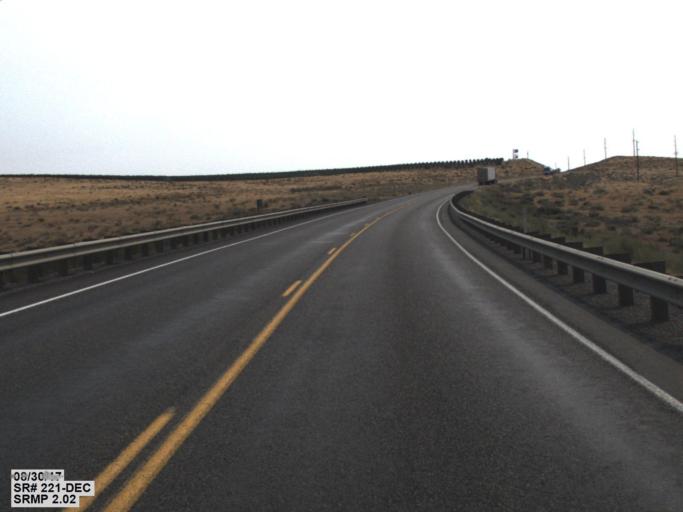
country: US
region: Oregon
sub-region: Morrow County
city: Irrigon
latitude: 45.9666
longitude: -119.6022
